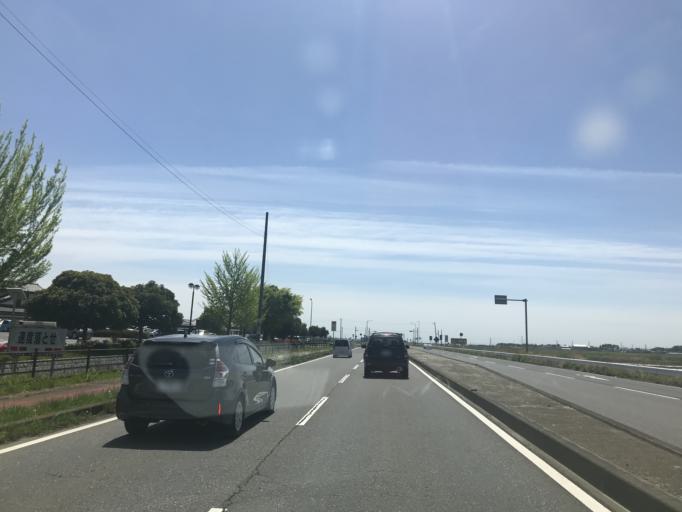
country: JP
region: Ibaraki
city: Shimodate
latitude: 36.2172
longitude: 139.9861
